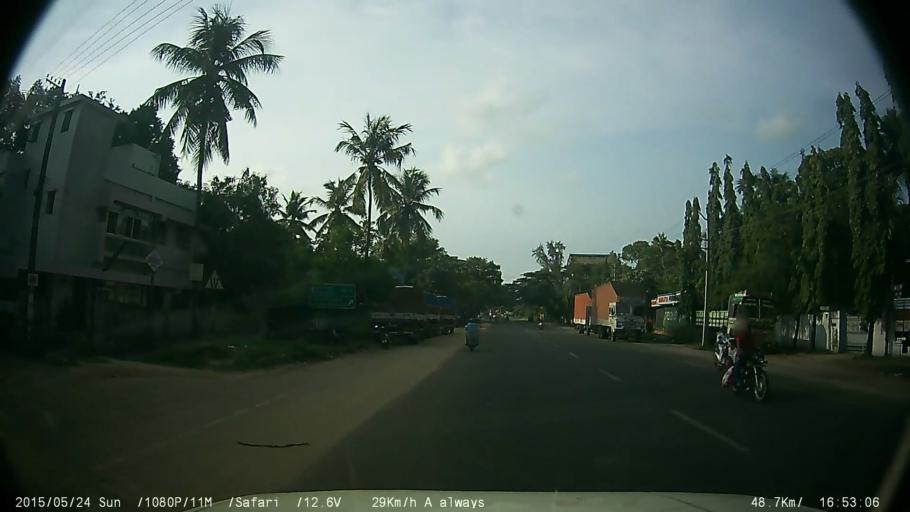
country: IN
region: Kerala
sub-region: Alappuzha
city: Shertallai
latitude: 9.6712
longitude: 76.3397
